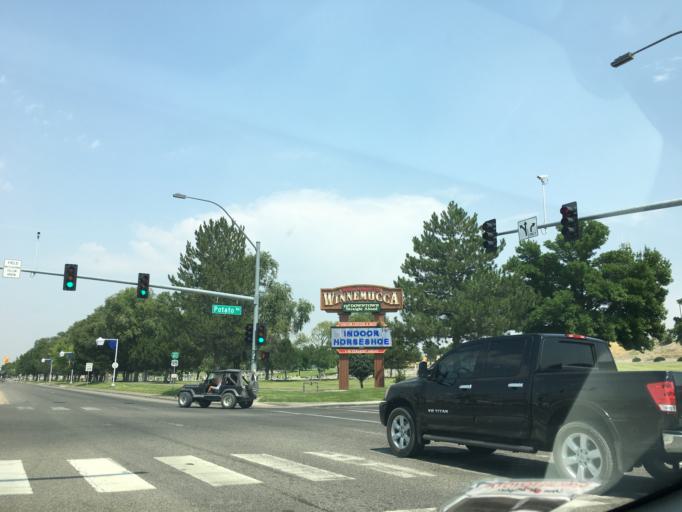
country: US
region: Nevada
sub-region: Humboldt County
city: Winnemucca
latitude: 40.9595
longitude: -117.7475
